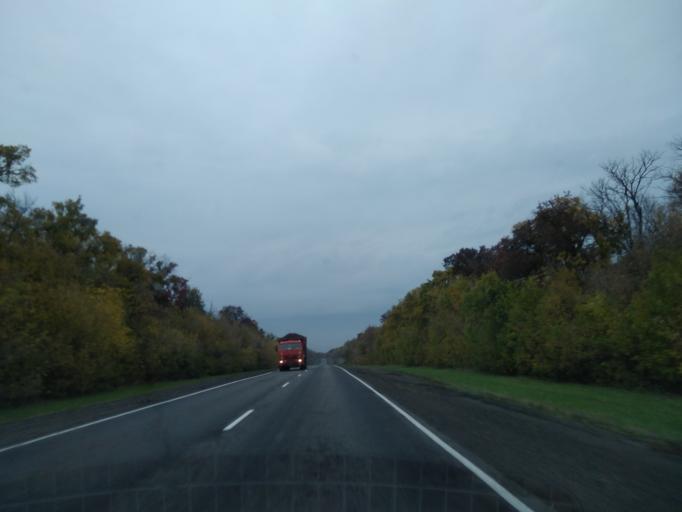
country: RU
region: Lipetsk
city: Zadonsk
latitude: 52.5081
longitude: 38.7577
